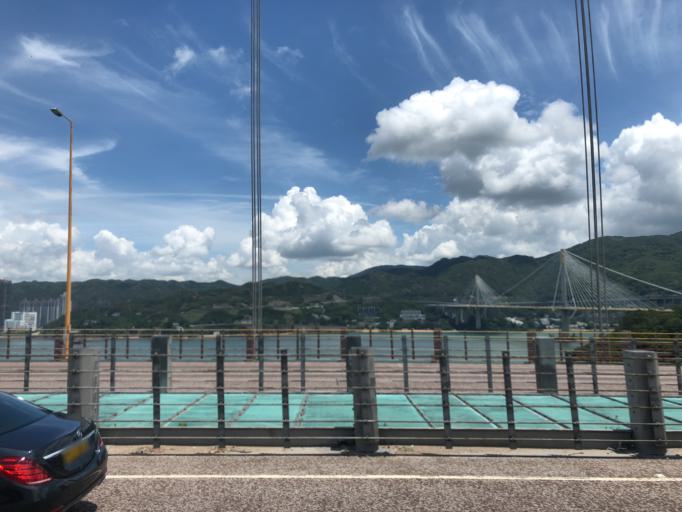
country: HK
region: Tsuen Wan
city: Tsuen Wan
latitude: 22.3523
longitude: 114.0789
